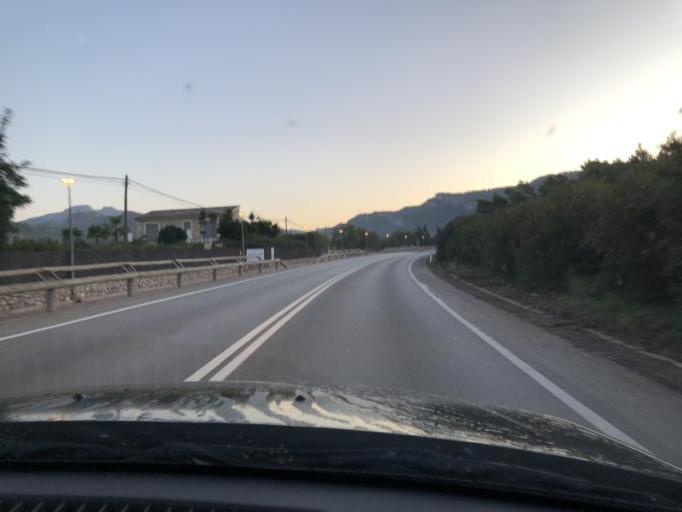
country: ES
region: Balearic Islands
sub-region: Illes Balears
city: Andratx
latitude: 39.5634
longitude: 2.4041
